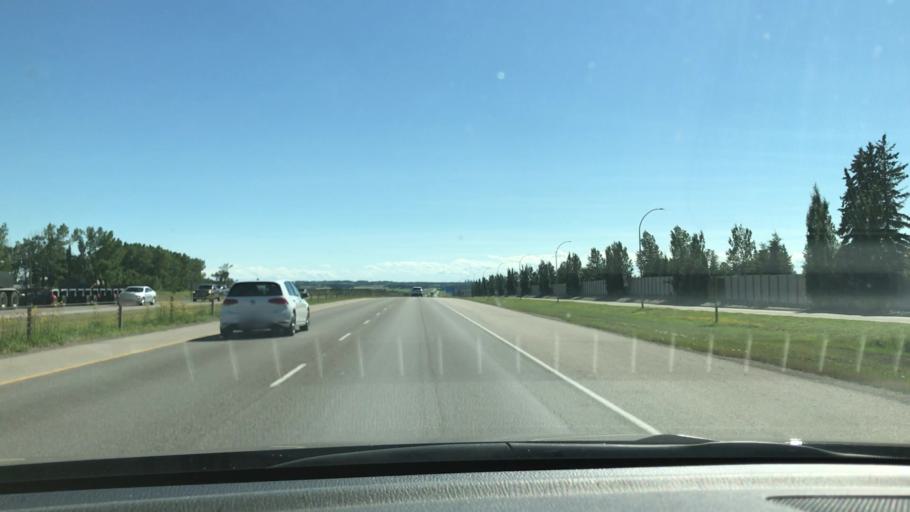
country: CA
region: Alberta
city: Penhold
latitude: 52.0143
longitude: -113.9469
